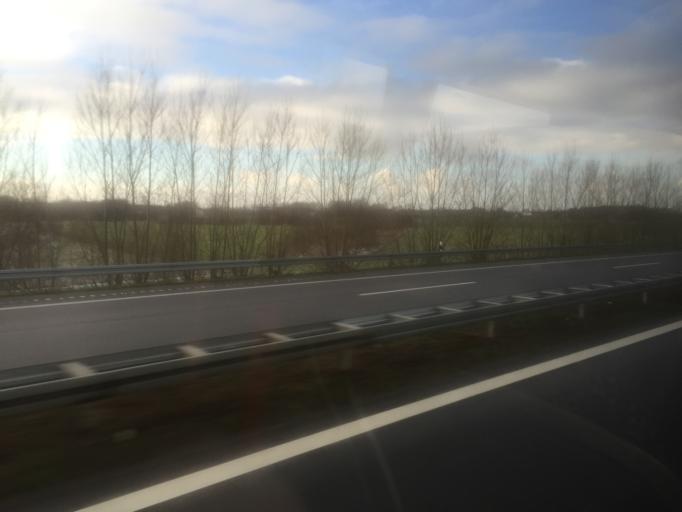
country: DE
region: Brandenburg
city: Dabergotz
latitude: 52.9156
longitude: 12.7230
